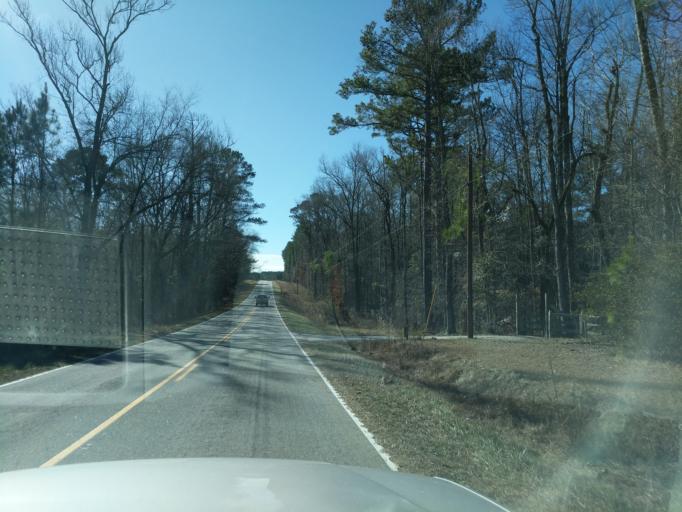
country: US
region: South Carolina
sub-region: Greenwood County
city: Ninety Six
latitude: 34.2078
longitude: -81.8842
